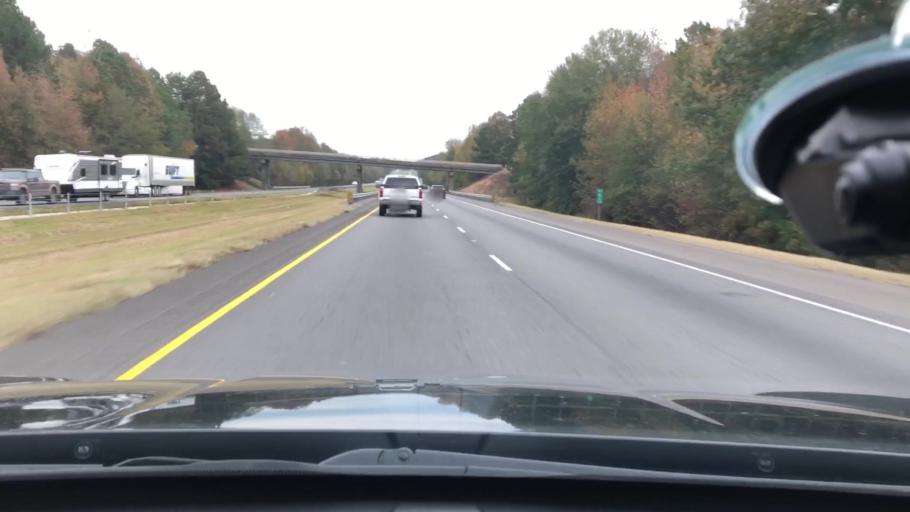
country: US
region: Arkansas
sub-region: Clark County
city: Gurdon
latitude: 34.0207
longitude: -93.1591
